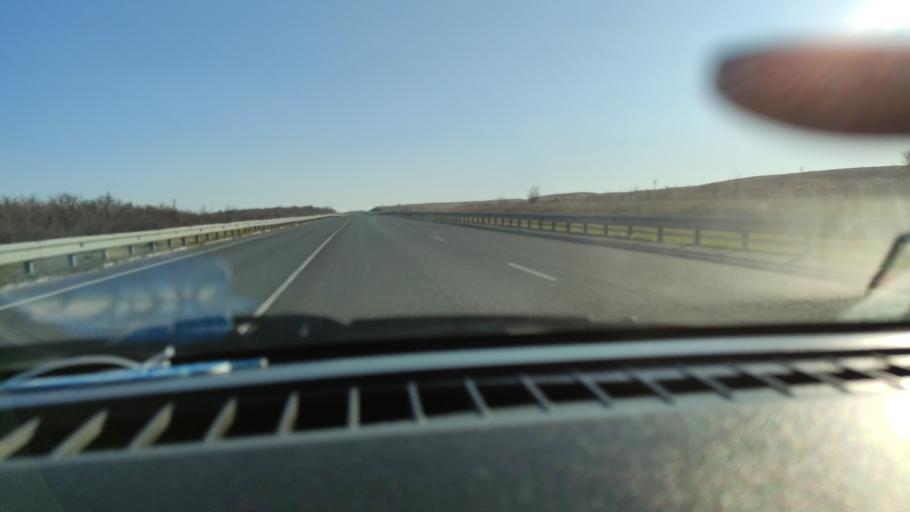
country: RU
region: Saratov
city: Alekseyevka
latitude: 52.2149
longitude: 47.8879
